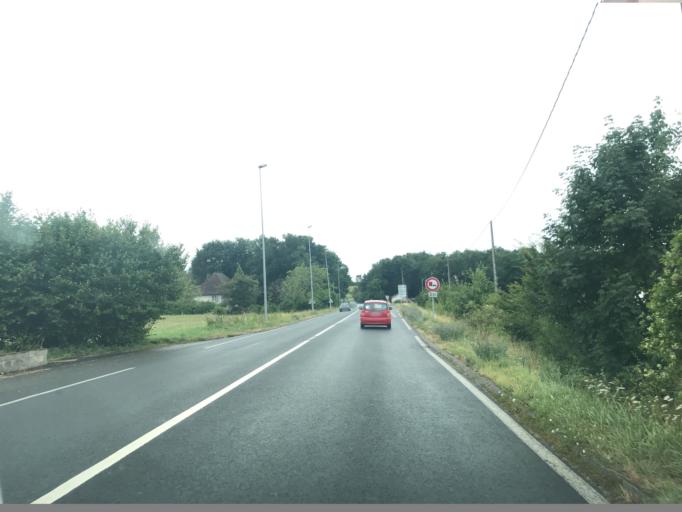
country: FR
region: Aquitaine
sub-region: Departement de la Dordogne
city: Brantome
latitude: 45.3006
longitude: 0.6608
